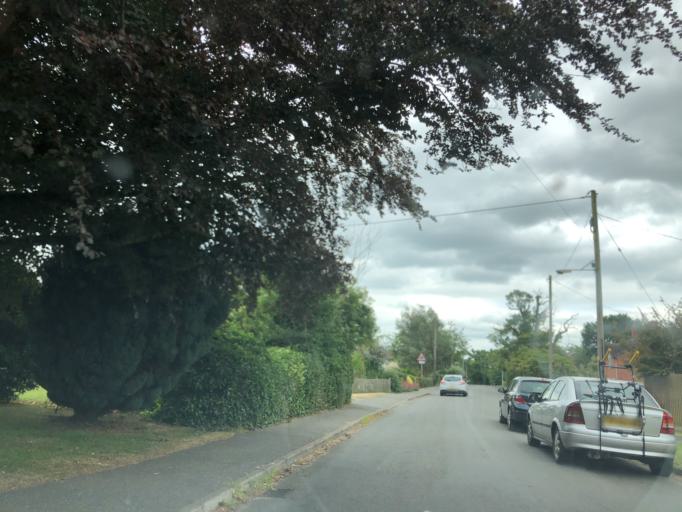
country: GB
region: England
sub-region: Suffolk
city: Thurston
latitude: 52.2506
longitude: 0.8177
